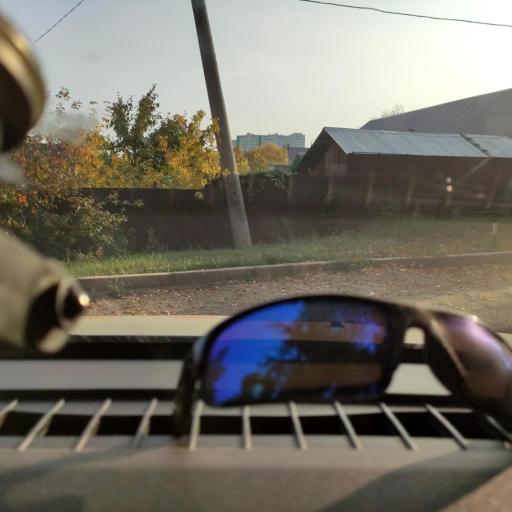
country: RU
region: Samara
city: Samara
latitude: 53.2000
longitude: 50.2084
